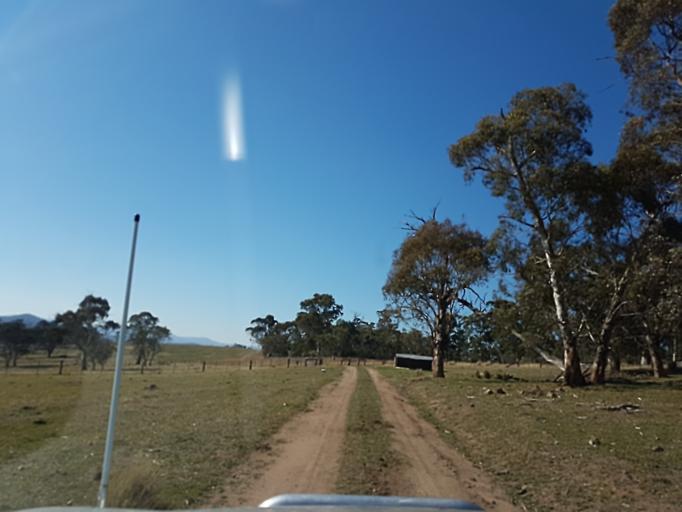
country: AU
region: New South Wales
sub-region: Snowy River
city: Jindabyne
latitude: -37.0418
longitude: 148.2839
